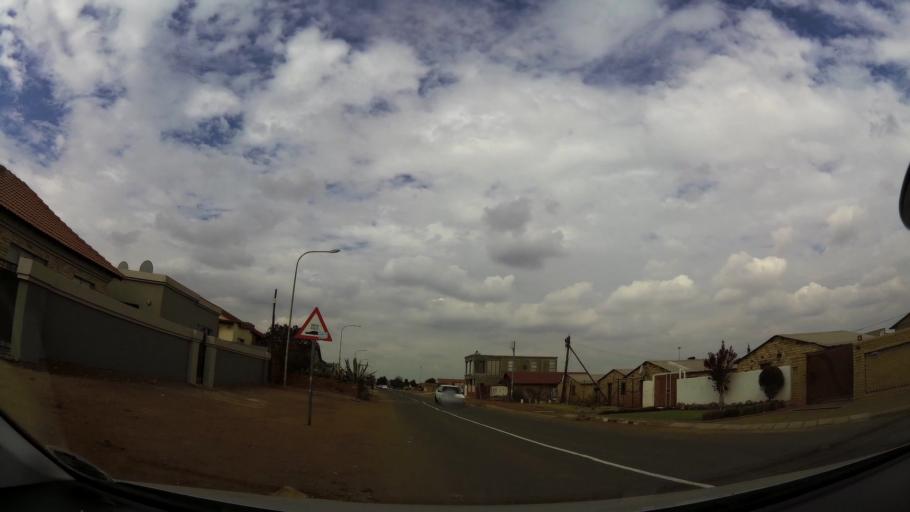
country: ZA
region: Gauteng
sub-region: City of Johannesburg Metropolitan Municipality
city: Soweto
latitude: -26.2759
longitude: 27.8481
